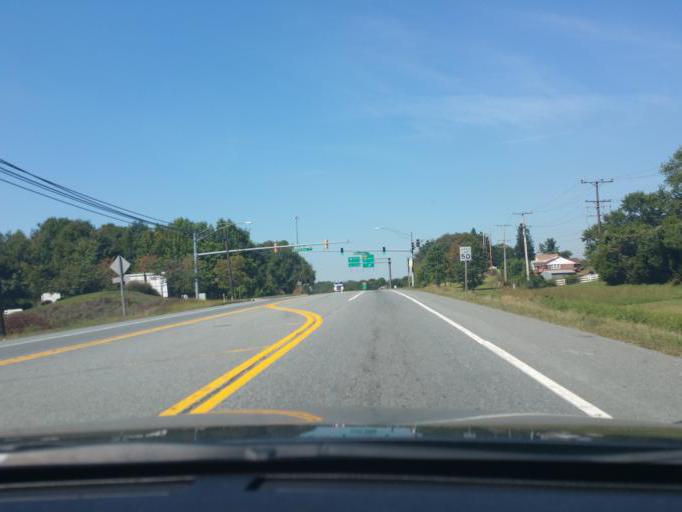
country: US
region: Maryland
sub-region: Harford County
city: Havre de Grace
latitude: 39.5676
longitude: -76.1300
